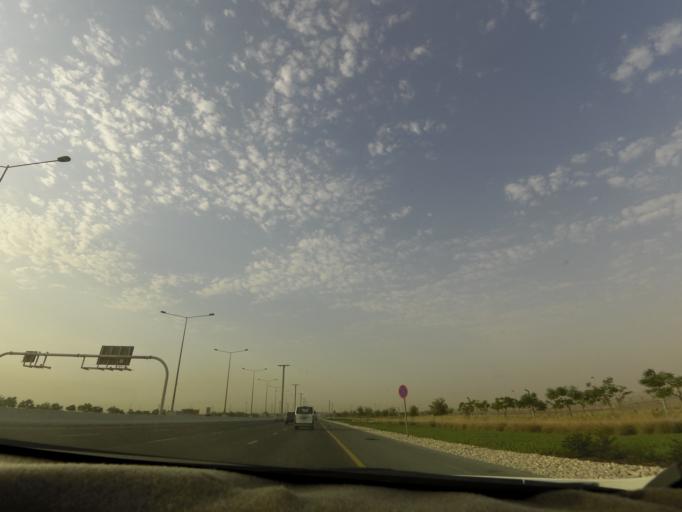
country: QA
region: Baladiyat ad Dawhah
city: Doha
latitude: 25.2494
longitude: 51.5873
